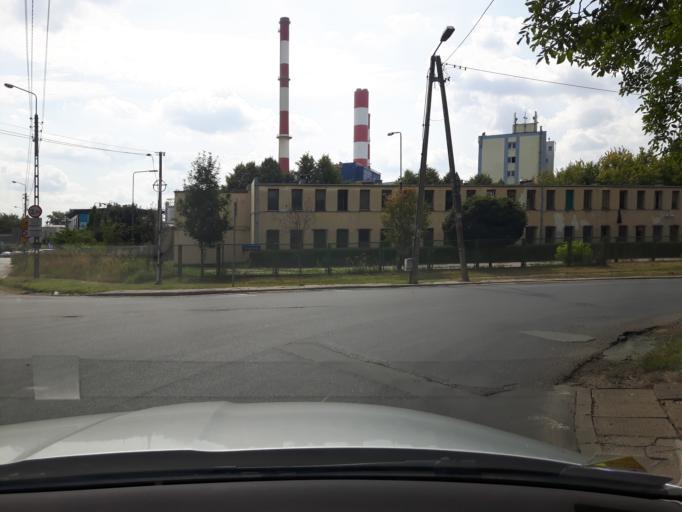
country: PL
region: Masovian Voivodeship
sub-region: Warszawa
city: Wilanow
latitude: 52.1948
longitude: 21.0880
